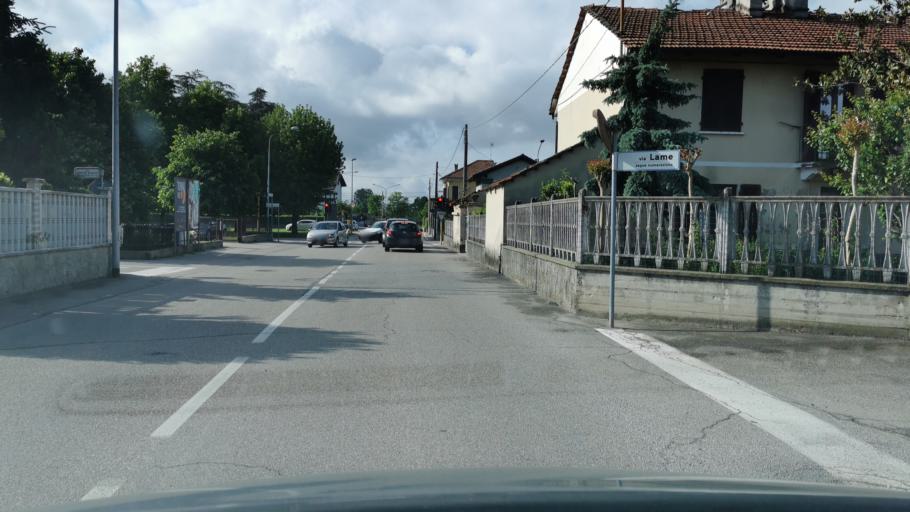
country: IT
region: Piedmont
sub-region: Provincia di Torino
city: Cambiano
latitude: 44.9677
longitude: 7.7807
